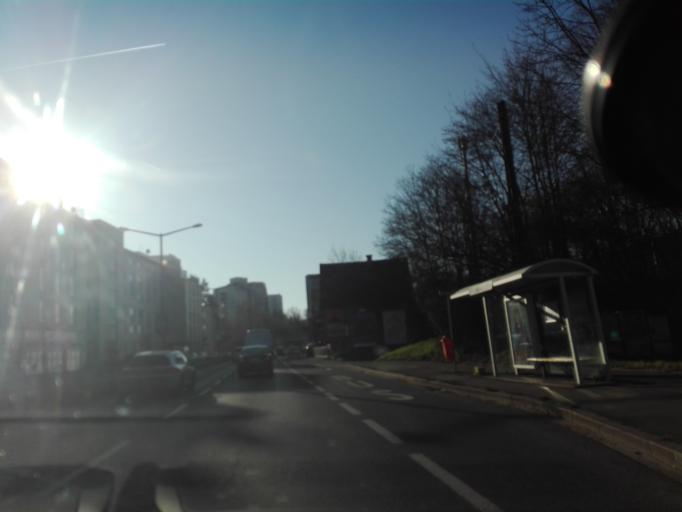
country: AT
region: Upper Austria
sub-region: Politischer Bezirk Linz-Land
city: Leonding
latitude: 48.2773
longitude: 14.2766
